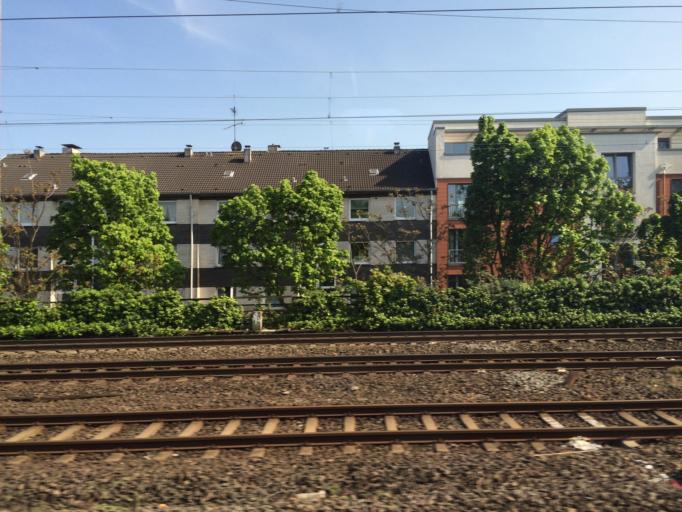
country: DE
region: North Rhine-Westphalia
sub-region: Regierungsbezirk Dusseldorf
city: Duisburg
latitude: 51.4376
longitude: 6.7845
